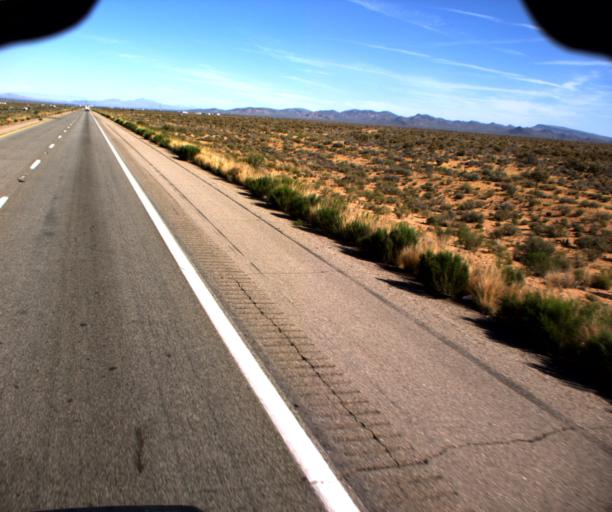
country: US
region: Arizona
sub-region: Mohave County
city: Dolan Springs
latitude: 35.4840
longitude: -114.3207
